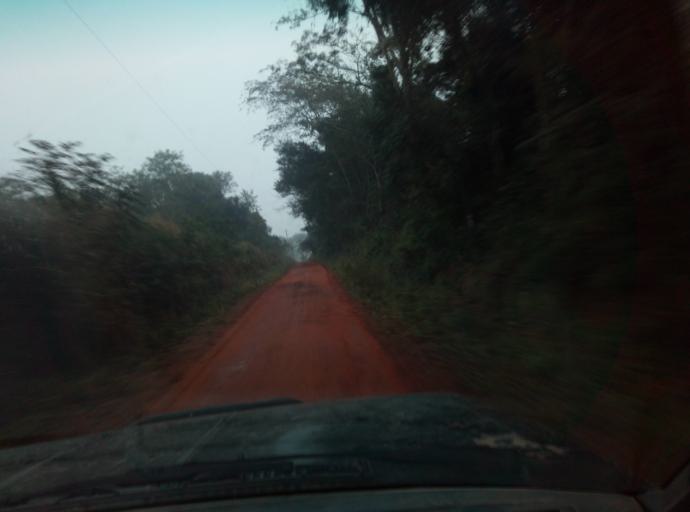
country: PY
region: Caaguazu
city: Doctor Cecilio Baez
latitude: -25.1580
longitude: -56.2699
